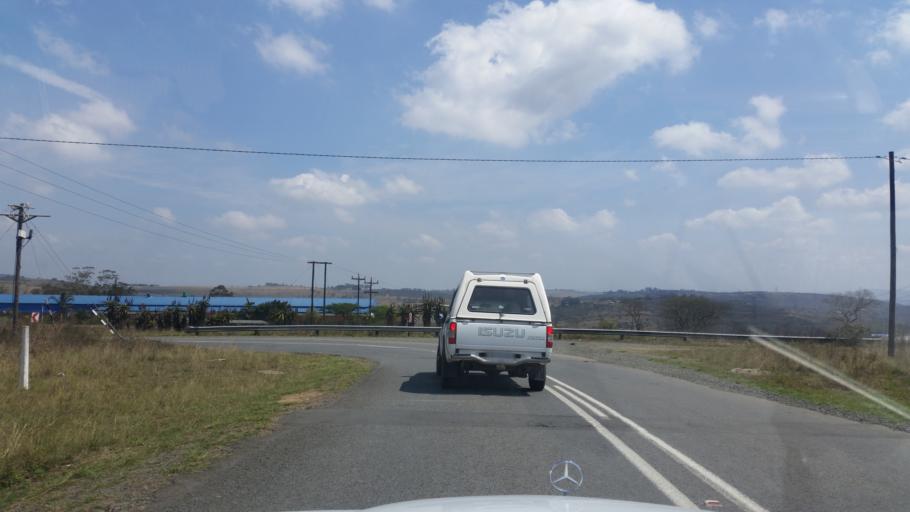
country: ZA
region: KwaZulu-Natal
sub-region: uMgungundlovu District Municipality
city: Camperdown
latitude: -29.7003
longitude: 30.4910
